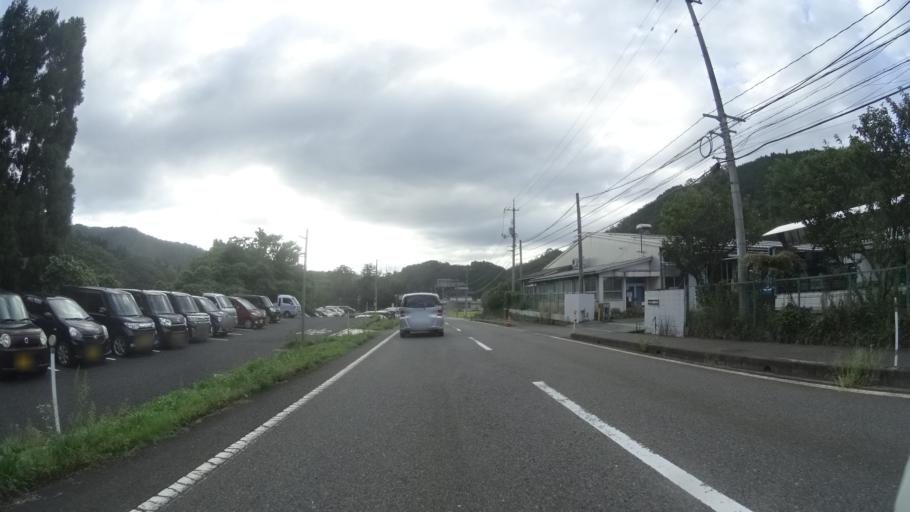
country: JP
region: Tottori
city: Kurayoshi
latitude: 35.4112
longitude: 133.9193
